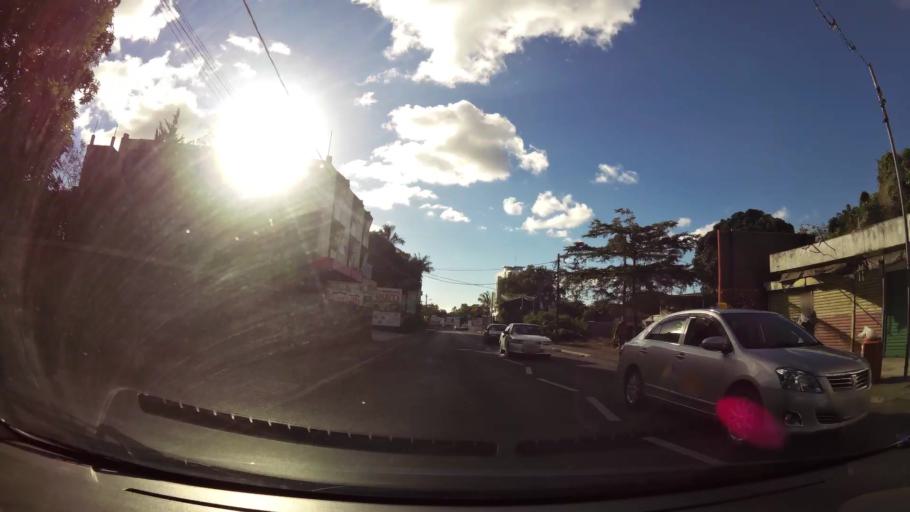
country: MU
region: Plaines Wilhems
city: Ebene
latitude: -20.2496
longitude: 57.4834
